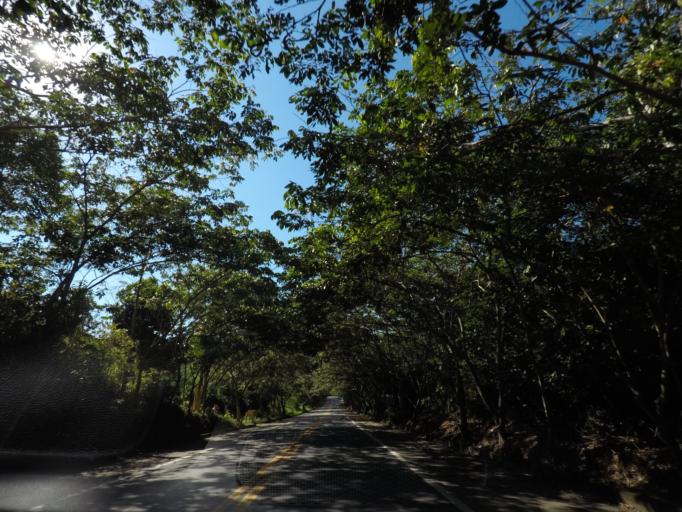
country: BR
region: Rio de Janeiro
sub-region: Parati
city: Paraty
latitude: -23.2627
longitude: -44.6863
